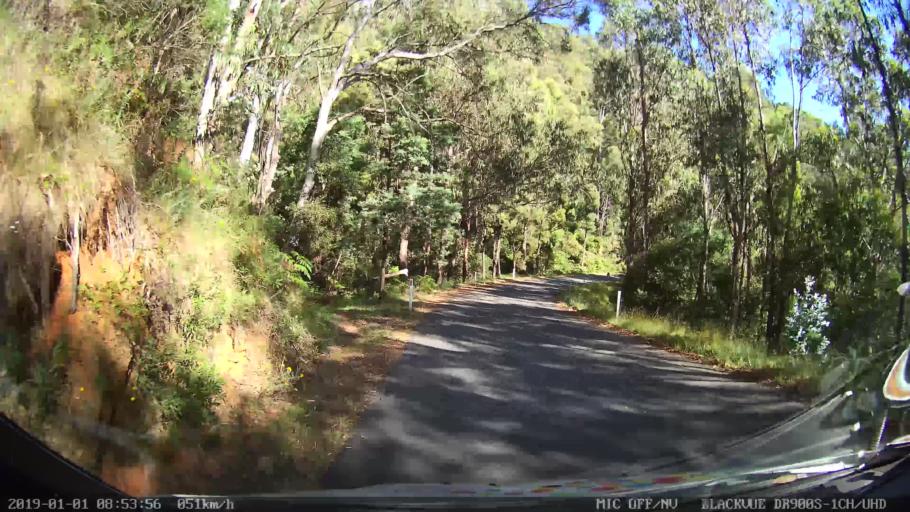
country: AU
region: New South Wales
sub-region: Snowy River
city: Jindabyne
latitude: -36.2625
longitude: 148.1897
